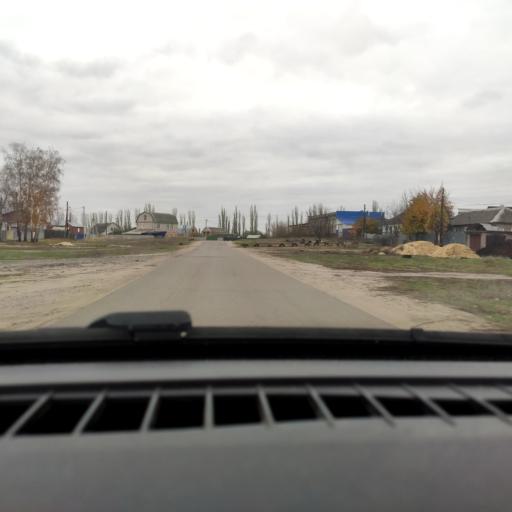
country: RU
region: Voronezj
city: Maslovka
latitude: 51.5786
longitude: 39.3039
